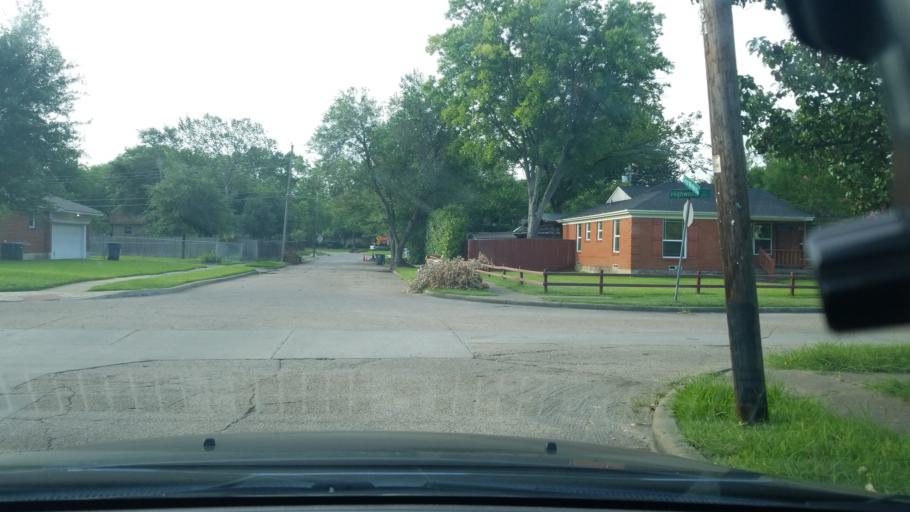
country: US
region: Texas
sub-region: Dallas County
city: Garland
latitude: 32.8298
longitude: -96.6659
